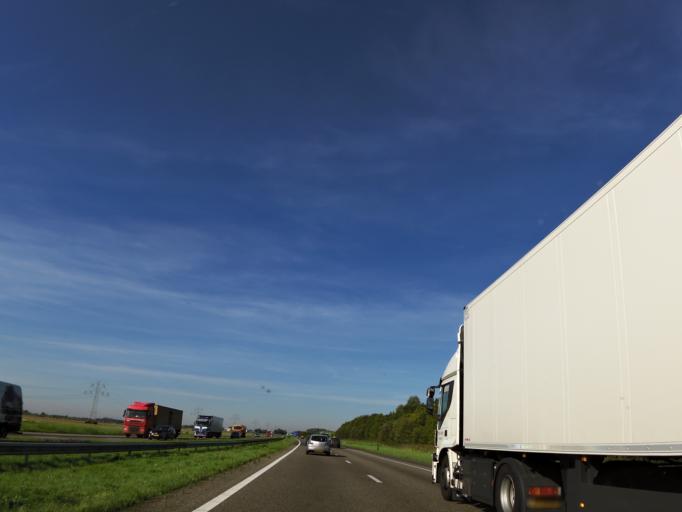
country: NL
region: North Brabant
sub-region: Gemeente Woensdrecht
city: Woensdrecht
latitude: 51.4264
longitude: 4.2173
